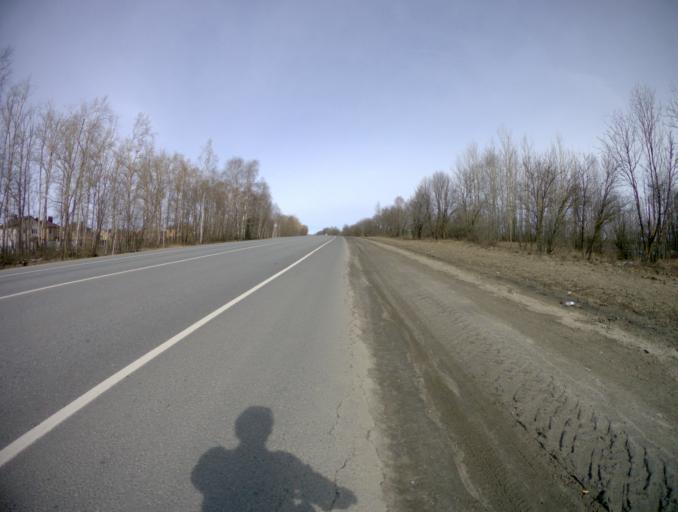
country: RU
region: Vladimir
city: Bogolyubovo
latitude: 56.1996
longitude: 40.4459
